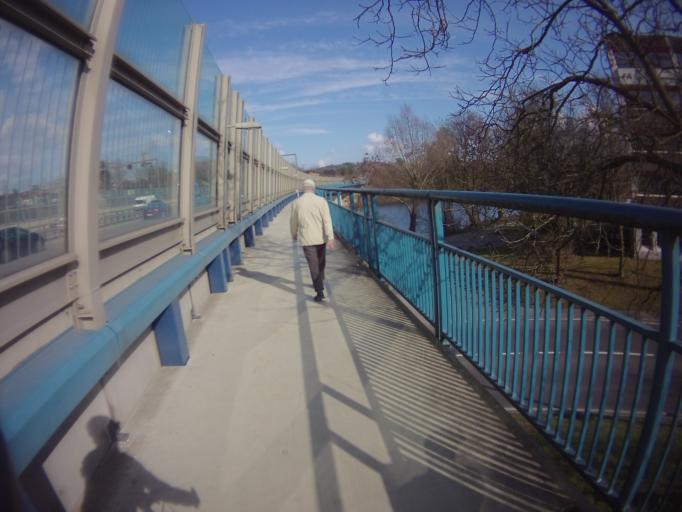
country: CH
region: Aargau
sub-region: Bezirk Baden
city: Neuenhof
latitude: 47.4545
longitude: 8.3305
